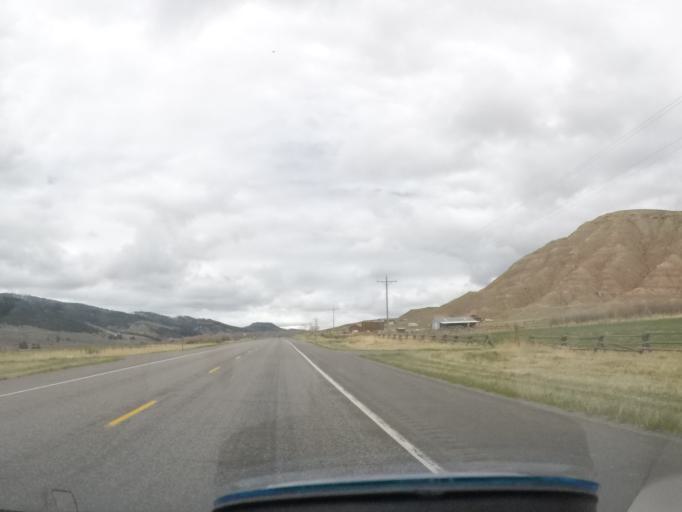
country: US
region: Wyoming
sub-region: Sublette County
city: Pinedale
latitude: 43.5700
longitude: -109.7165
